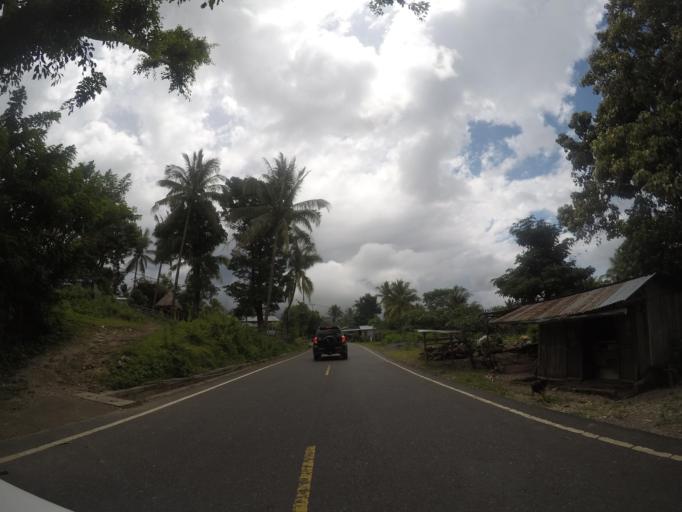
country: TL
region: Bobonaro
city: Maliana
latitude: -8.9634
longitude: 125.0538
